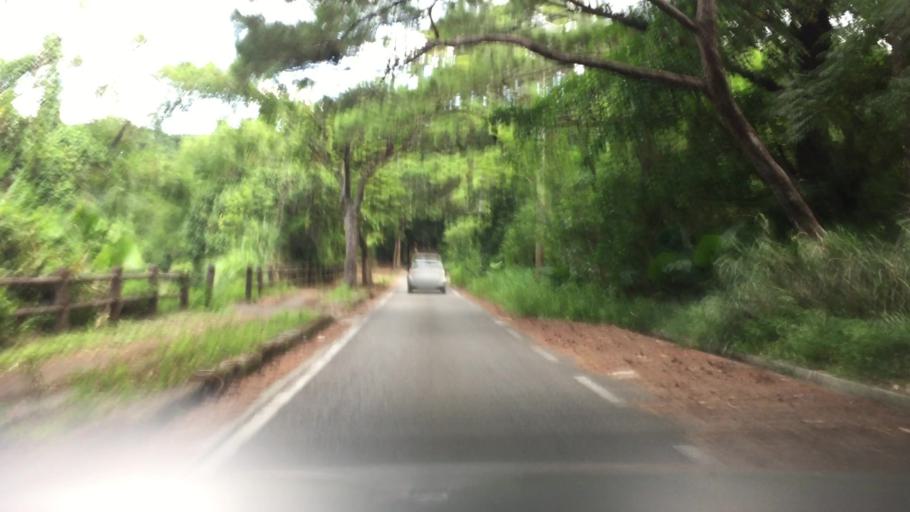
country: JP
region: Okinawa
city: Ishigaki
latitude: 24.4521
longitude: 124.1371
